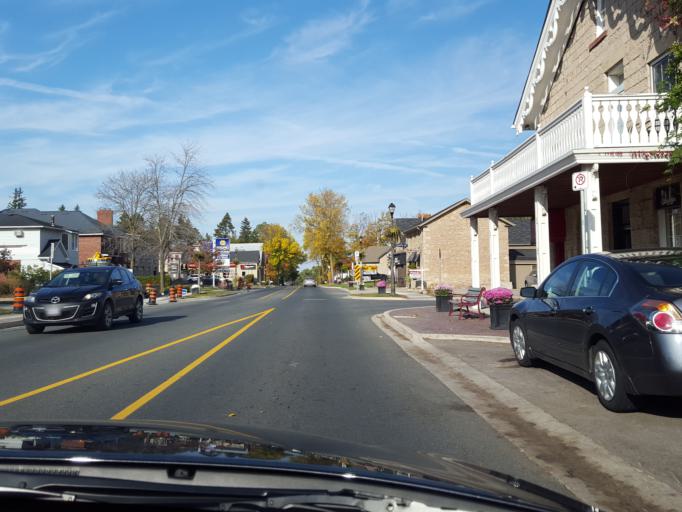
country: CA
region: Ontario
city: Ancaster
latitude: 43.2279
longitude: -79.9756
